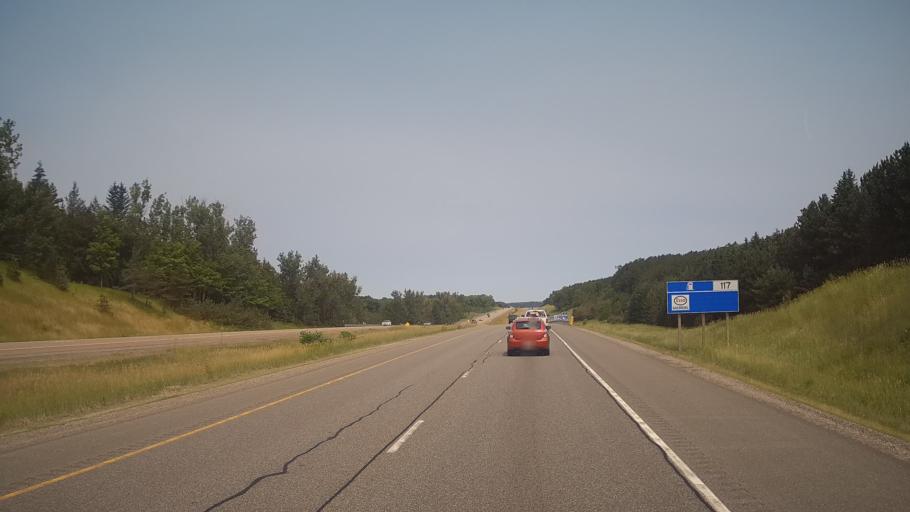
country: CA
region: Ontario
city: Barrie
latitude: 44.4995
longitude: -79.7170
